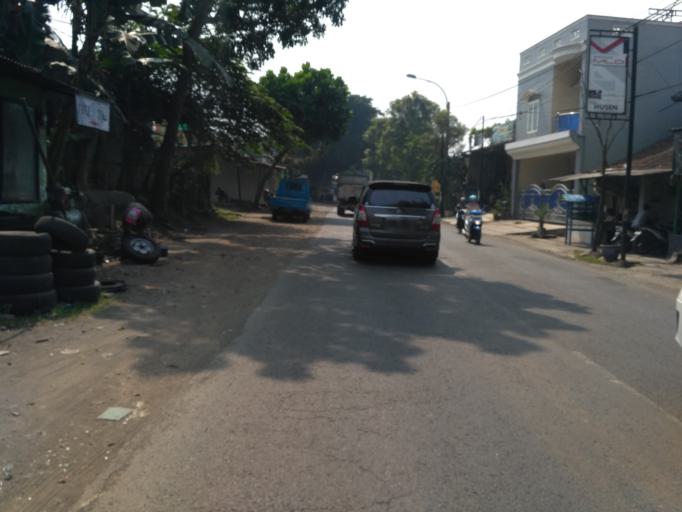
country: ID
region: East Java
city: Malang
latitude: -7.9875
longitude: 112.6534
